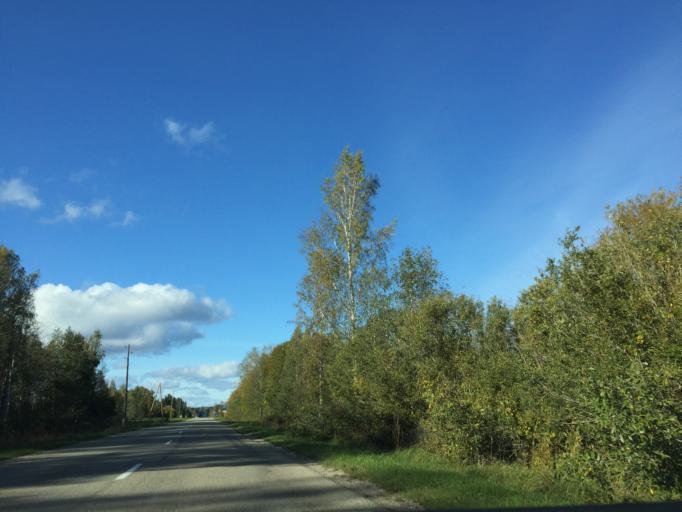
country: LV
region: Rojas
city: Roja
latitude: 57.4476
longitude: 22.8988
